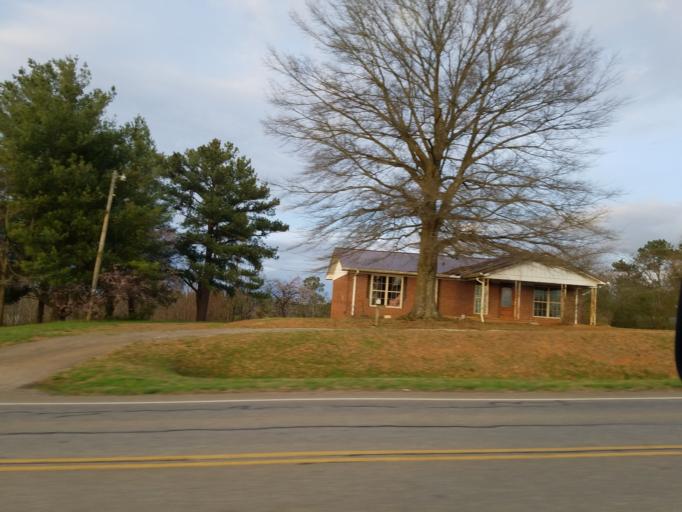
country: US
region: Georgia
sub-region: Pickens County
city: Jasper
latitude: 34.4752
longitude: -84.5258
